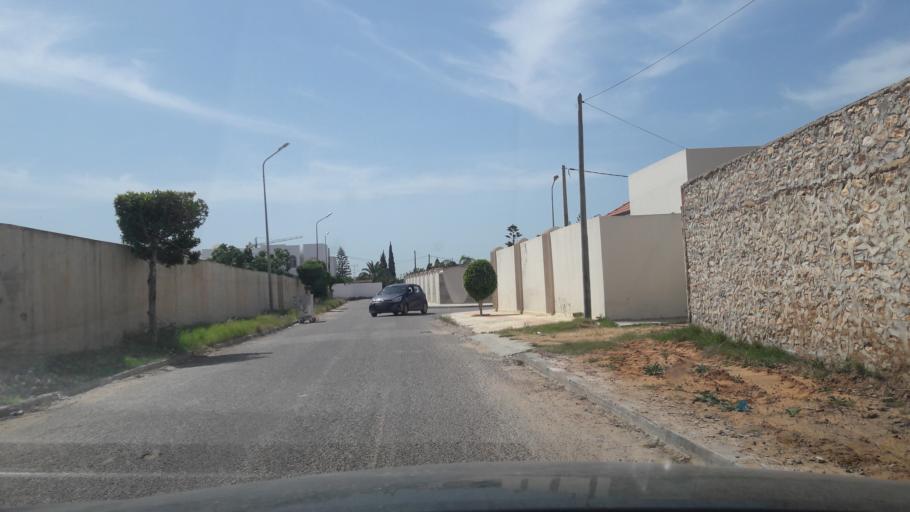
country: TN
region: Safaqis
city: Al Qarmadah
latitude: 34.7897
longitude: 10.7571
